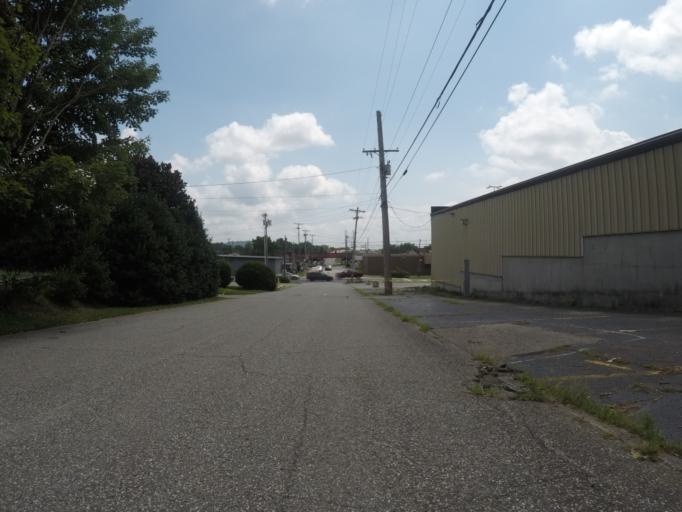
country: US
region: Kentucky
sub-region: Boyd County
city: Catlettsburg
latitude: 38.4048
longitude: -82.6018
